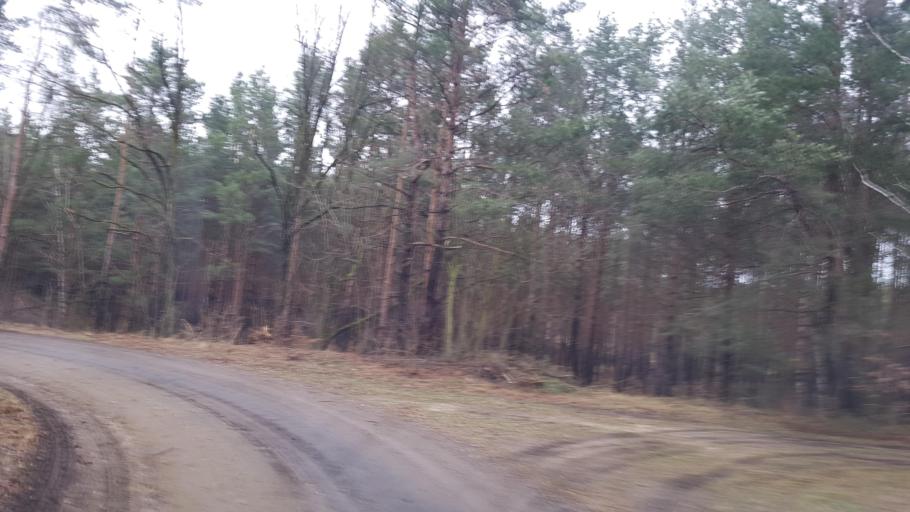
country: DE
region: Brandenburg
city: Altdobern
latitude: 51.6448
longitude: 14.0053
